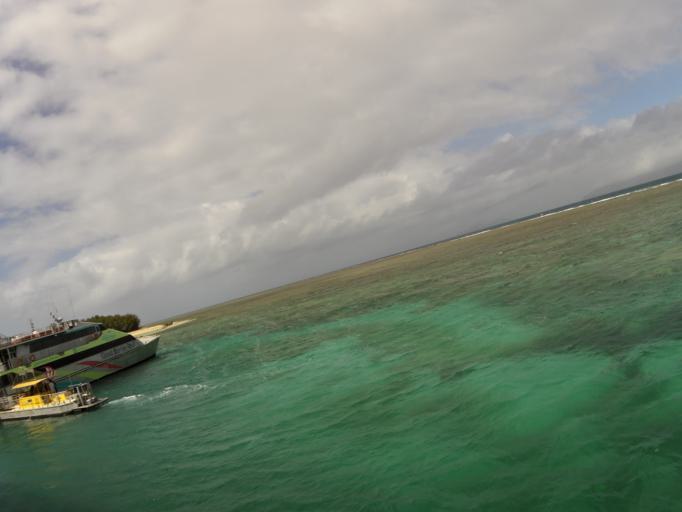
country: AU
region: Queensland
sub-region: Cairns
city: Yorkeys Knob
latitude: -16.7579
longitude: 145.9685
